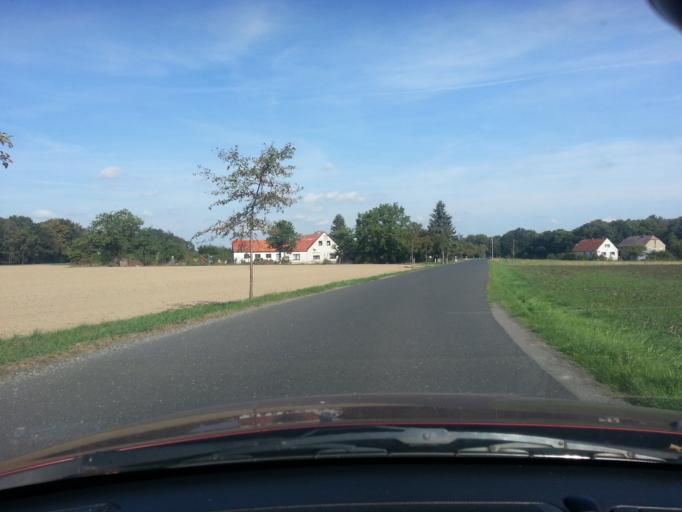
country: DE
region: Saxony
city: Reichenbach
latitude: 51.1109
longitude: 14.8326
